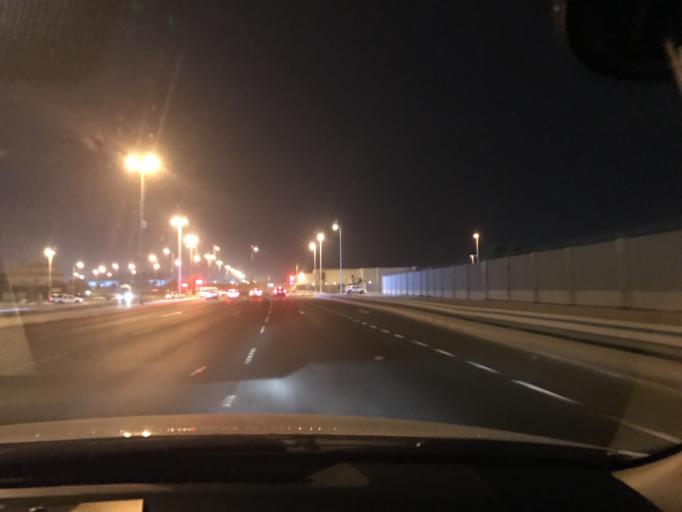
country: BH
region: Muharraq
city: Al Hadd
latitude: 26.2614
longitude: 50.6421
